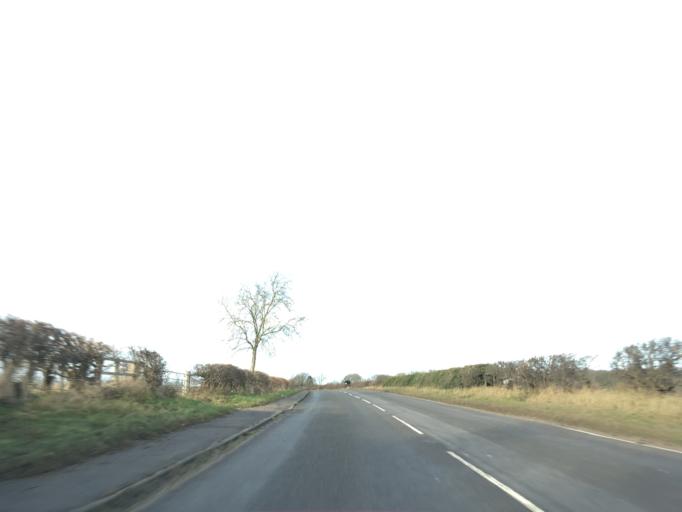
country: GB
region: England
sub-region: Nottinghamshire
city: South Collingham
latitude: 53.1551
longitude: -0.7580
